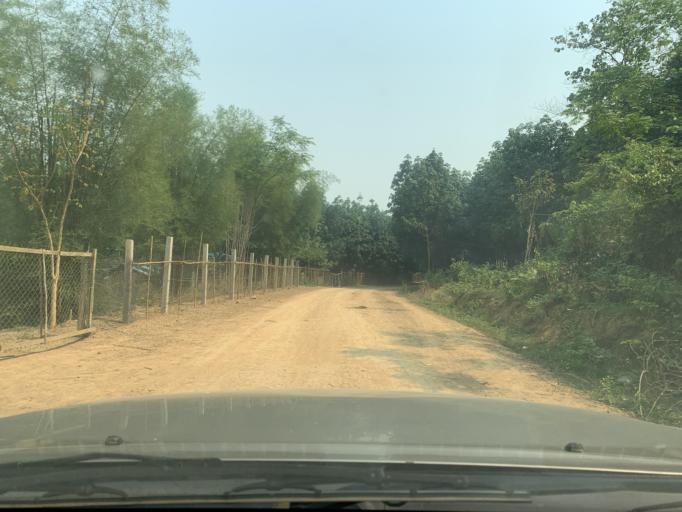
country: LA
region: Louangphabang
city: Xiang Ngeun
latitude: 19.7946
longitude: 102.1992
